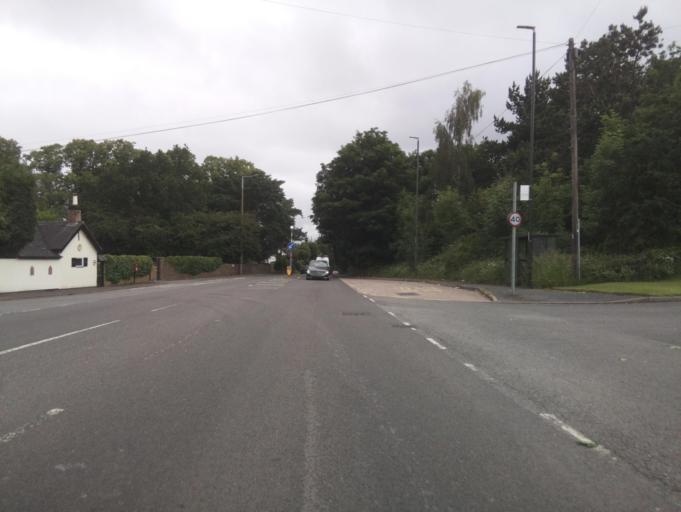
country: GB
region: England
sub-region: Derbyshire
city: Swadlincote
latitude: 52.7952
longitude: -1.5788
